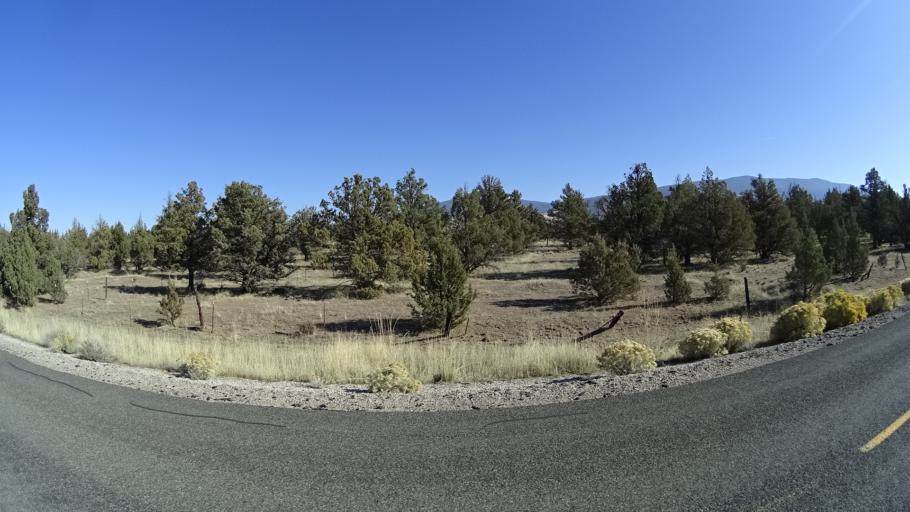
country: US
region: California
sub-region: Siskiyou County
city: Montague
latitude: 41.6601
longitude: -122.3671
